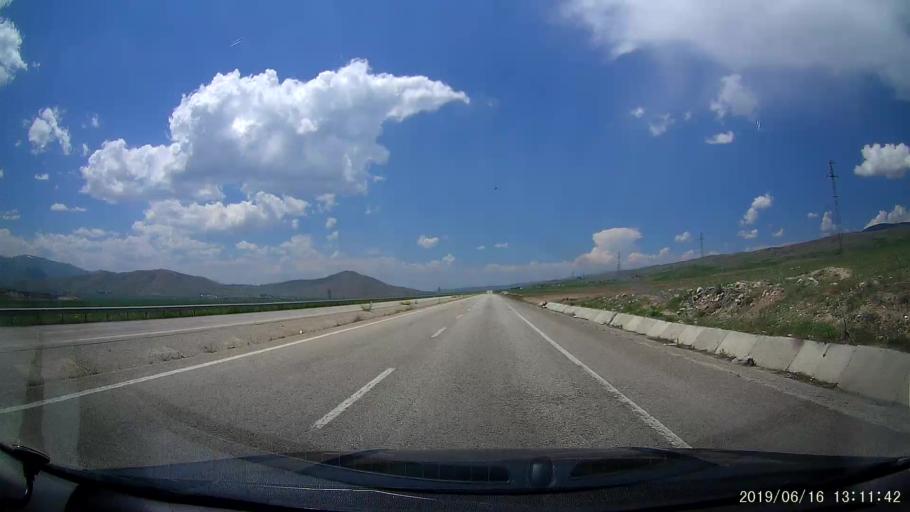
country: TR
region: Agri
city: Diyadin
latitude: 39.5930
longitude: 43.5998
